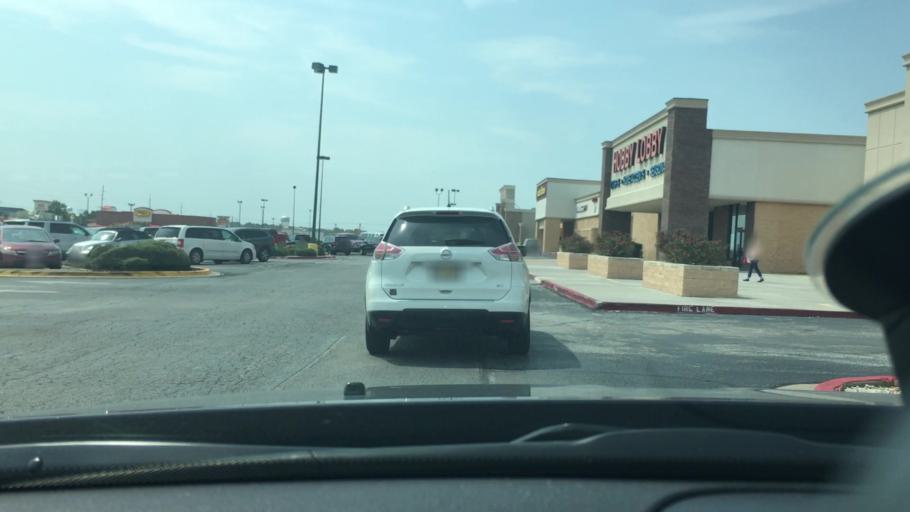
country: US
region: Oklahoma
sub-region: Carter County
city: Ardmore
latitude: 34.1908
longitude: -97.1443
